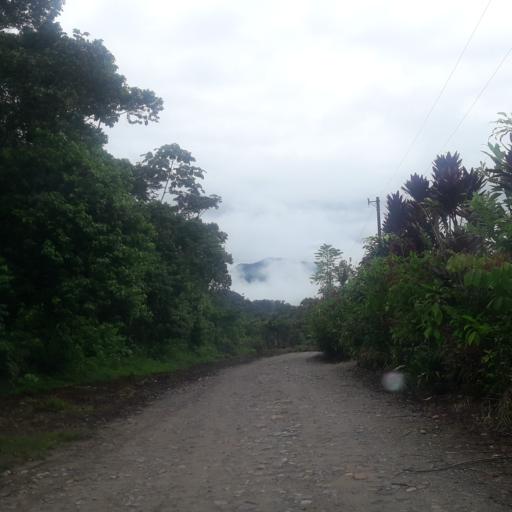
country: EC
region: Napo
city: Archidona
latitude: -0.9154
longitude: -77.8205
